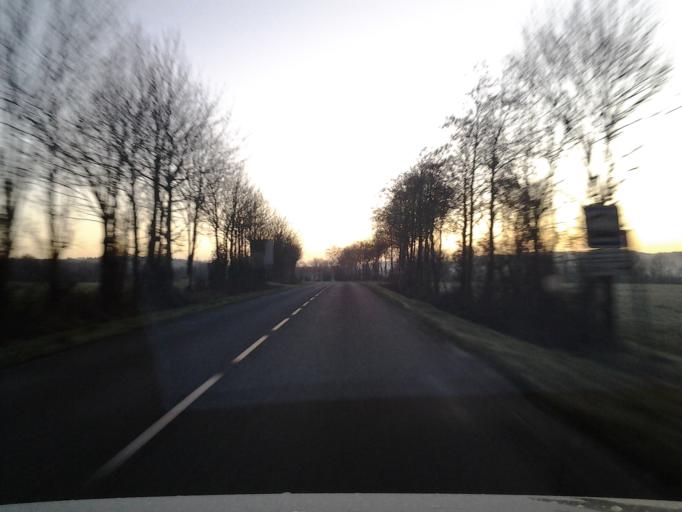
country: FR
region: Pays de la Loire
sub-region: Departement de la Vendee
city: Les Herbiers
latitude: 46.8700
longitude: -0.9699
